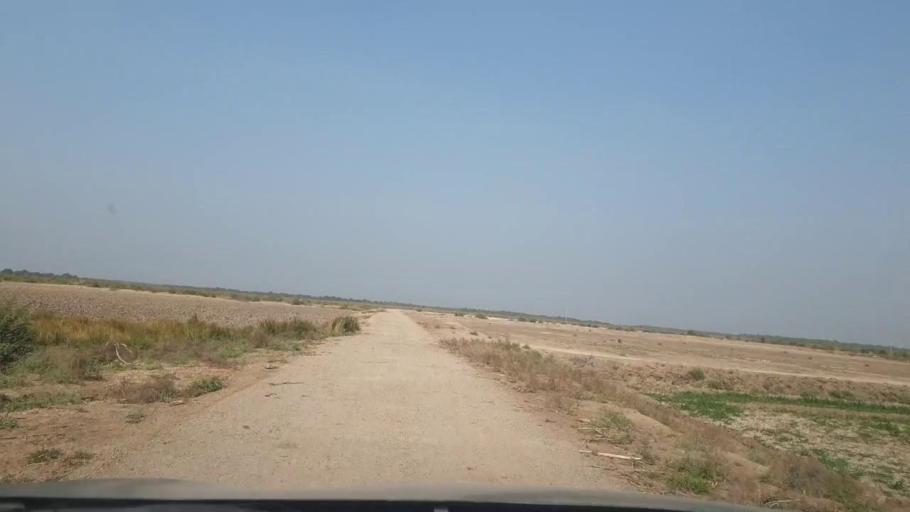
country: PK
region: Sindh
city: Tando Allahyar
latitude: 25.5682
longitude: 68.8256
